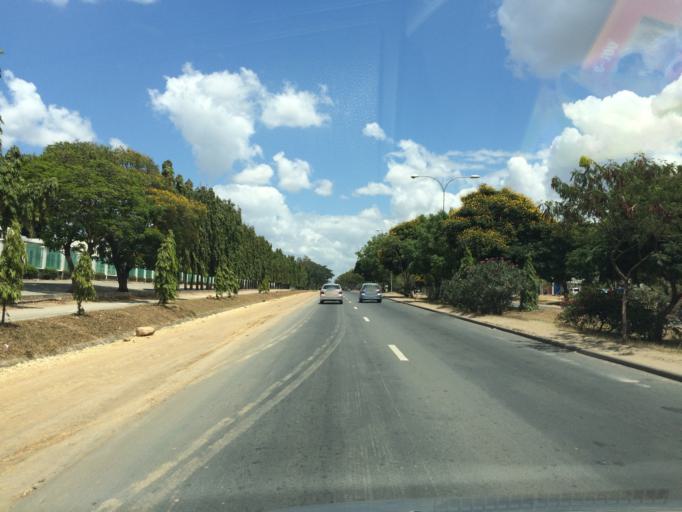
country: TZ
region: Dar es Salaam
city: Dar es Salaam
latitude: -6.8406
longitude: 39.2529
